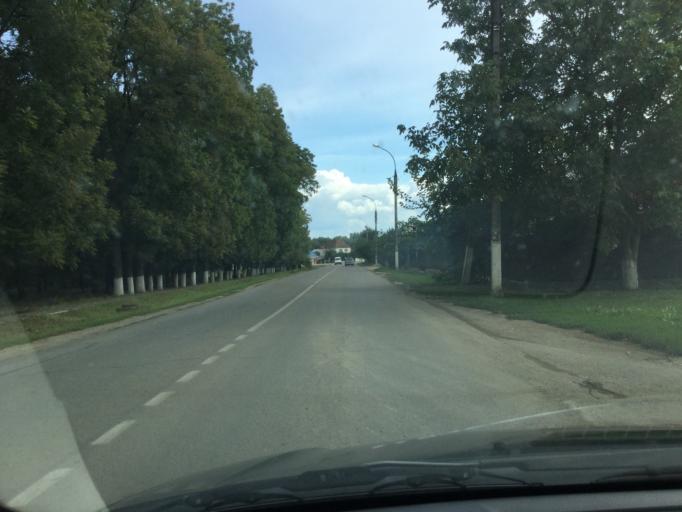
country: RU
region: Krasnodarskiy
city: Sovkhoznyy
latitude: 45.2837
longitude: 38.1099
